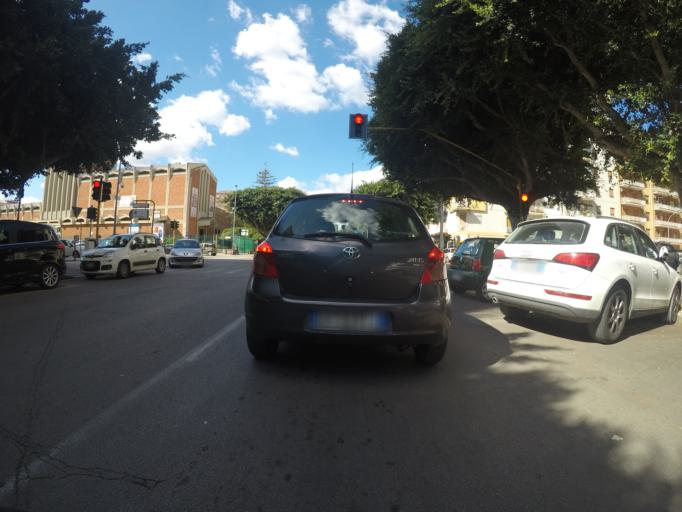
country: IT
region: Sicily
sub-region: Palermo
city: Palermo
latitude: 38.1439
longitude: 13.3621
